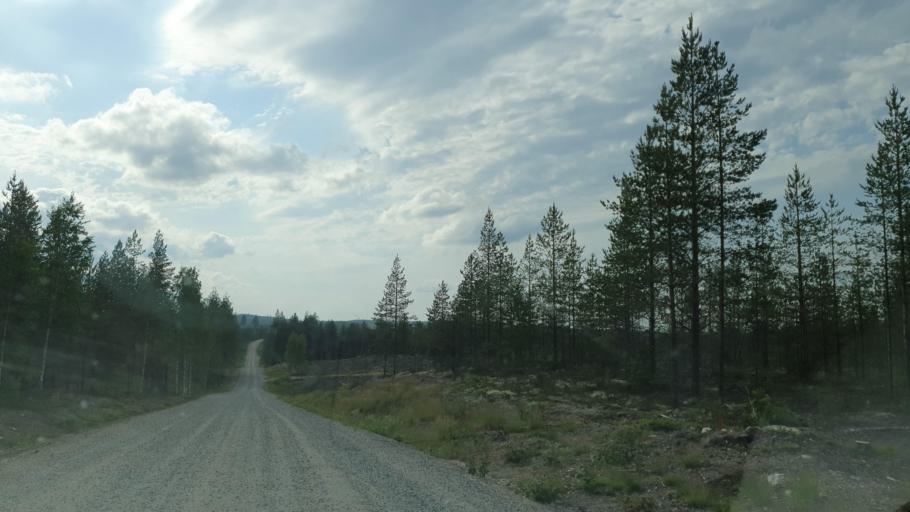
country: FI
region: Kainuu
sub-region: Kehys-Kainuu
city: Kuhmo
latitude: 64.0218
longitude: 29.8920
